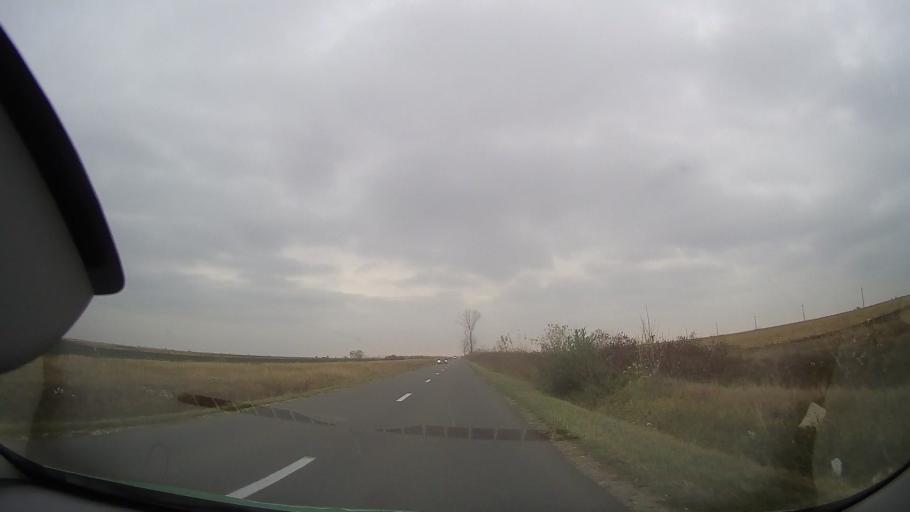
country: RO
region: Ialomita
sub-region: Comuna Garbovi
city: Garbovi
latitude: 44.7623
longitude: 26.7340
